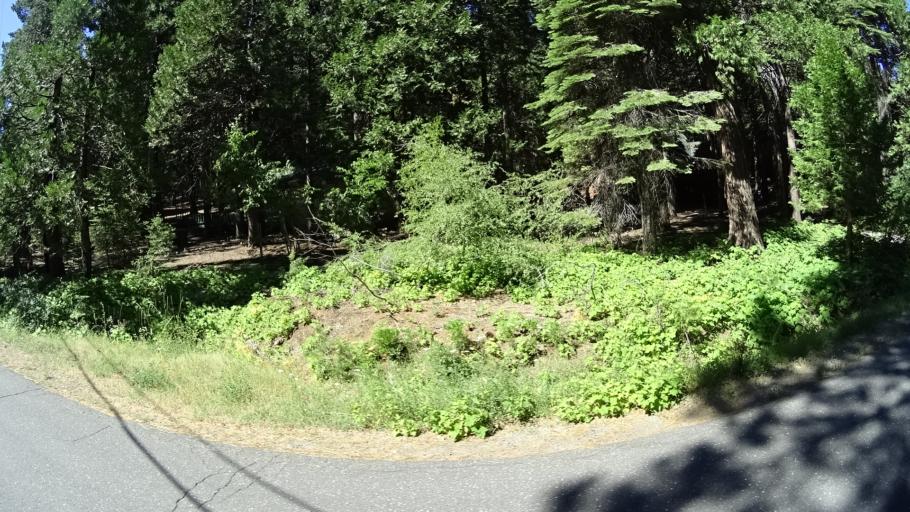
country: US
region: California
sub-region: Calaveras County
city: Arnold
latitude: 38.2851
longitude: -120.2769
